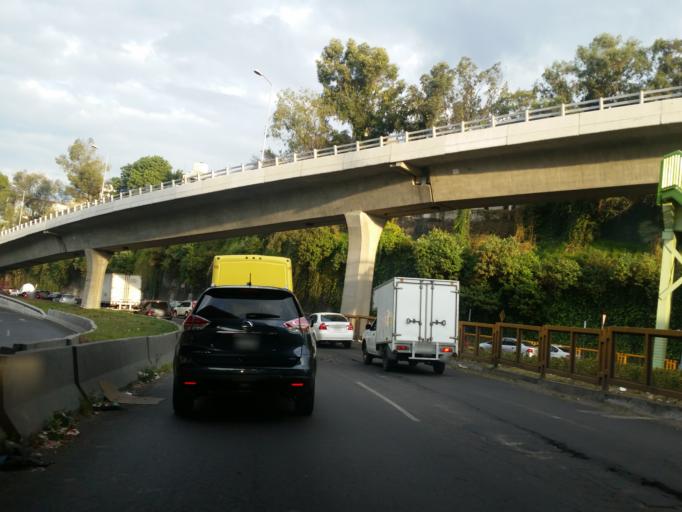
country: MX
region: Mexico City
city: Col. Bosques de las Lomas
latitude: 19.3869
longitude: -99.2434
